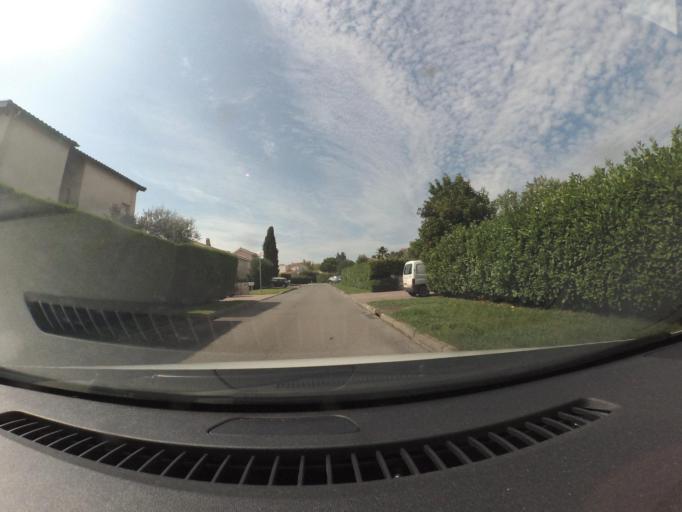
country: FR
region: Languedoc-Roussillon
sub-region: Departement de l'Herault
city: Baillargues
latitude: 43.6504
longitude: 4.0085
